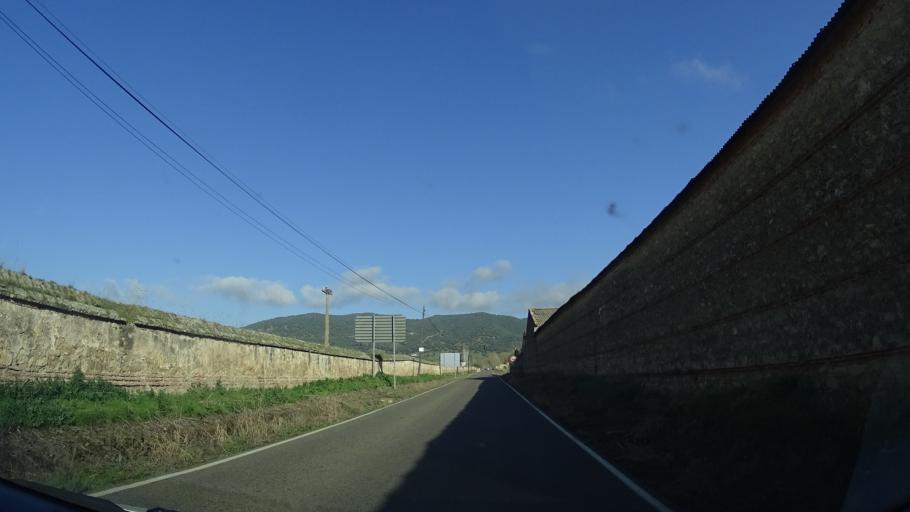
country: ES
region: Andalusia
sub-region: Province of Cordoba
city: Villarrubia
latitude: 37.8762
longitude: -4.8491
